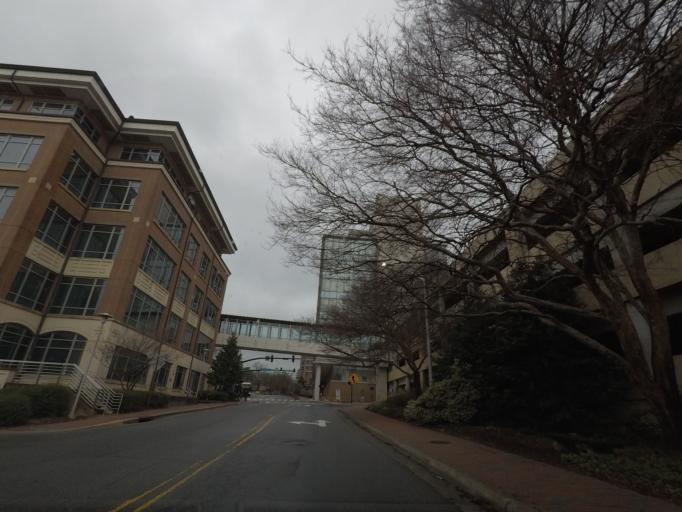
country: US
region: North Carolina
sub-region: Orange County
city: Chapel Hill
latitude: 35.9019
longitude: -79.0527
